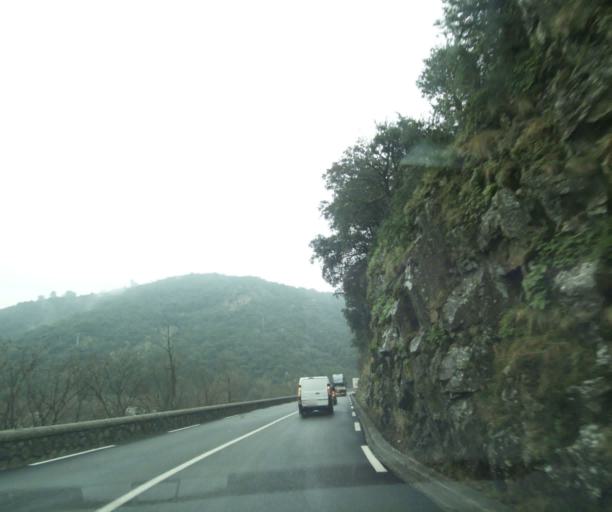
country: FR
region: Rhone-Alpes
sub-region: Departement de l'Ardeche
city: Jaujac
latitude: 44.6636
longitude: 4.2941
